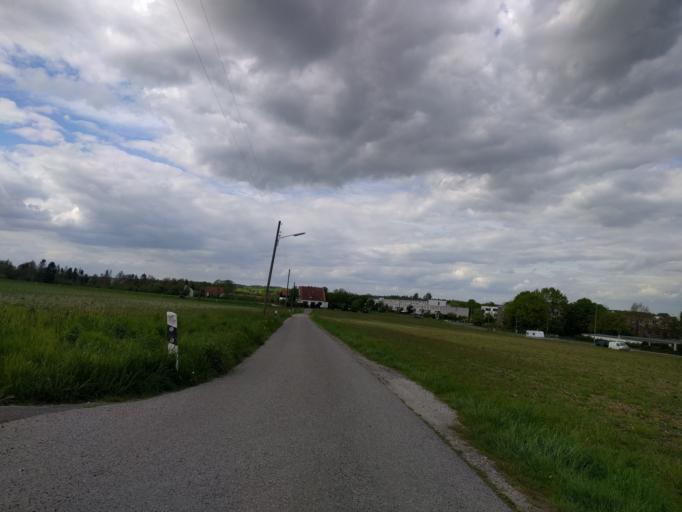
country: DE
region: North Rhine-Westphalia
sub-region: Regierungsbezirk Detmold
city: Bielefeld
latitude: 52.0463
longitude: 8.5008
